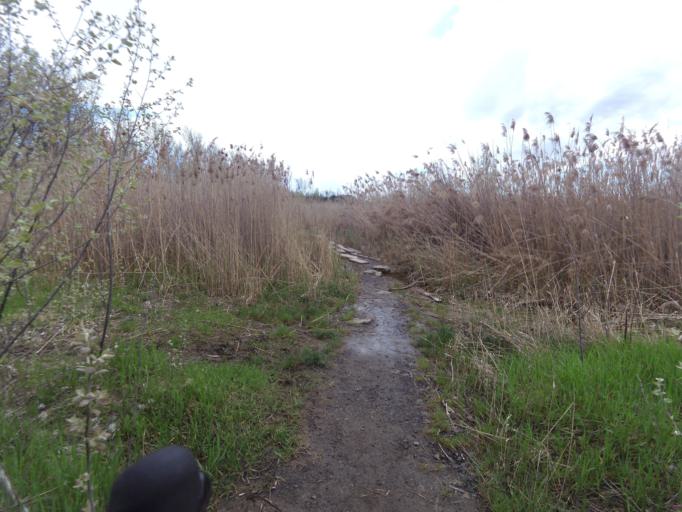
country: CA
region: Ontario
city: Bells Corners
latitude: 45.2743
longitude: -75.7963
